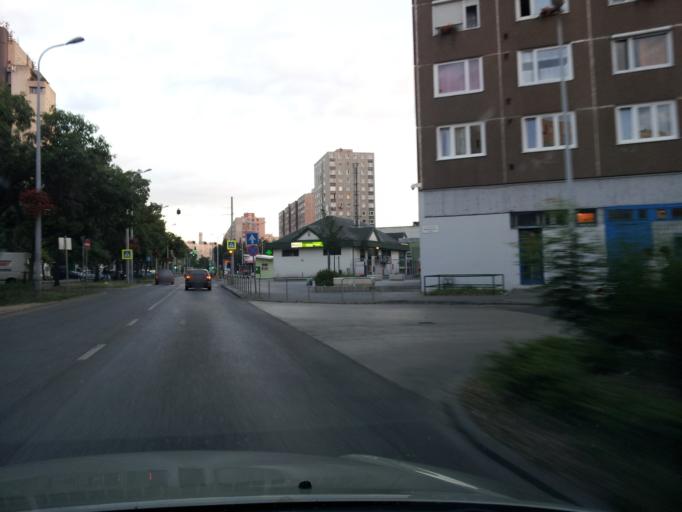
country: HU
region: Budapest
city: Budapest XV. keruelet
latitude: 47.5463
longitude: 19.1401
